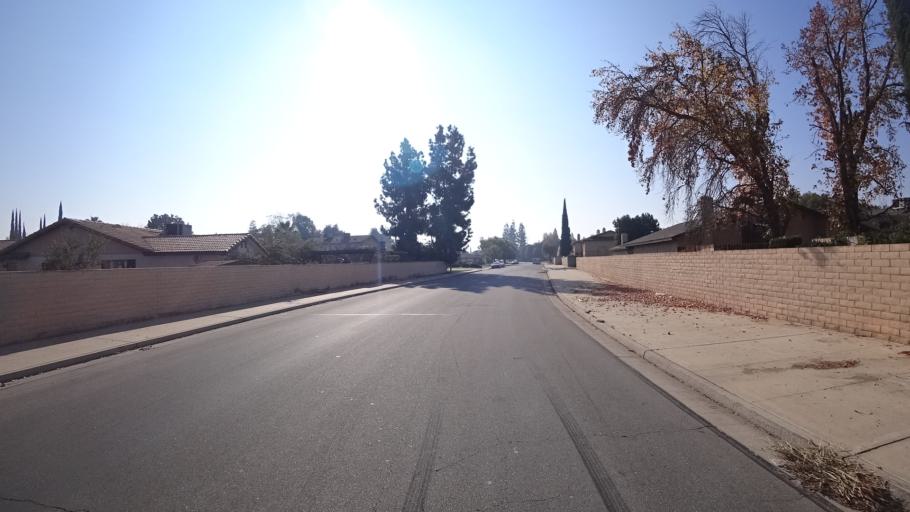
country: US
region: California
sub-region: Kern County
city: Greenacres
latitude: 35.3614
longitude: -119.0887
